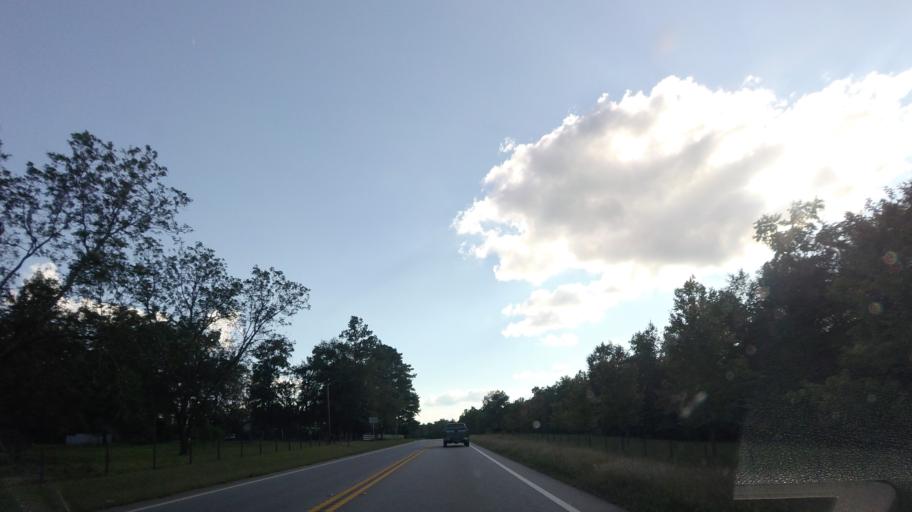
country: US
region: Georgia
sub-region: Upson County
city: Thomaston
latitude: 32.9272
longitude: -84.2778
